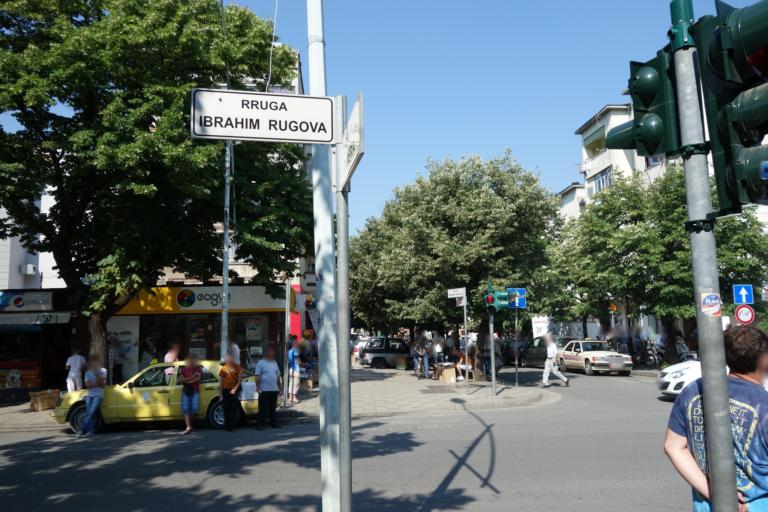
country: AL
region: Tirane
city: Tirana
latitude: 41.3273
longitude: 19.8166
